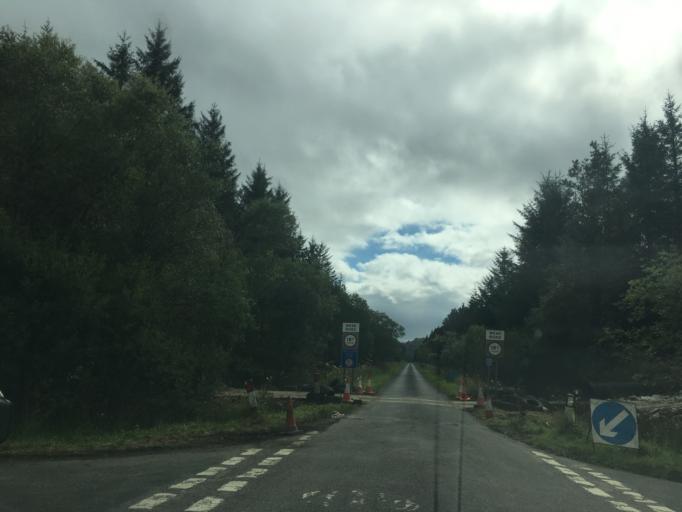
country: GB
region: Scotland
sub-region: Argyll and Bute
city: Lochgilphead
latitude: 56.0955
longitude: -5.5118
